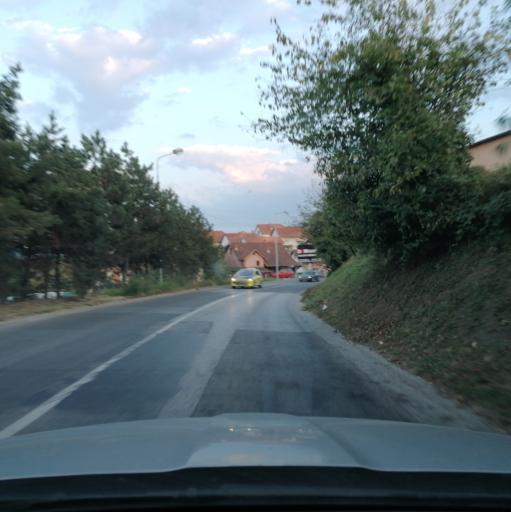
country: RS
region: Central Serbia
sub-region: Raski Okrug
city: Kraljevo
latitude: 43.7361
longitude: 20.6792
